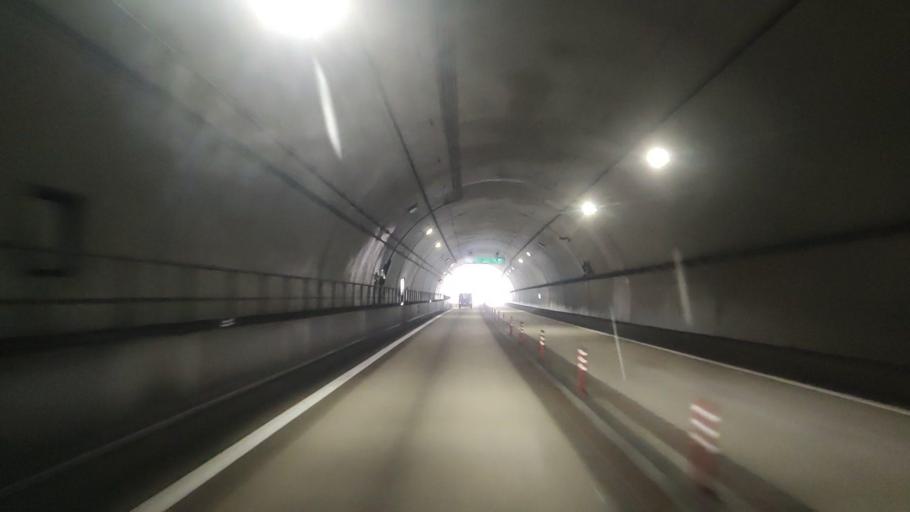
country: JP
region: Wakayama
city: Tanabe
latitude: 33.5525
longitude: 135.5127
